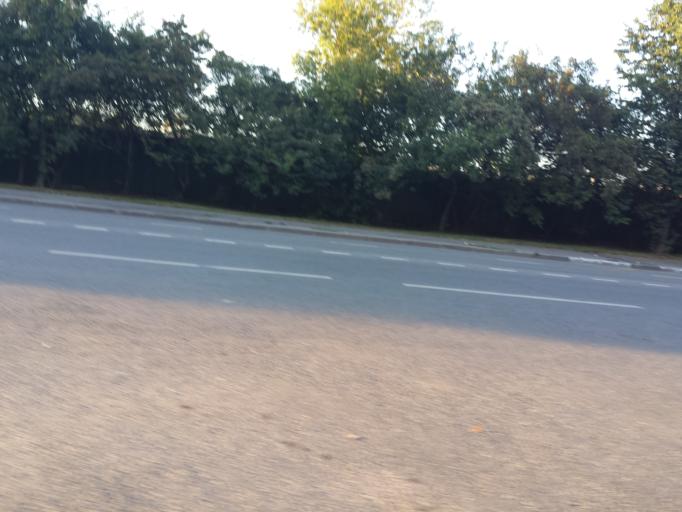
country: RU
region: Moscow
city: Davydkovo
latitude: 55.7262
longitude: 37.4458
